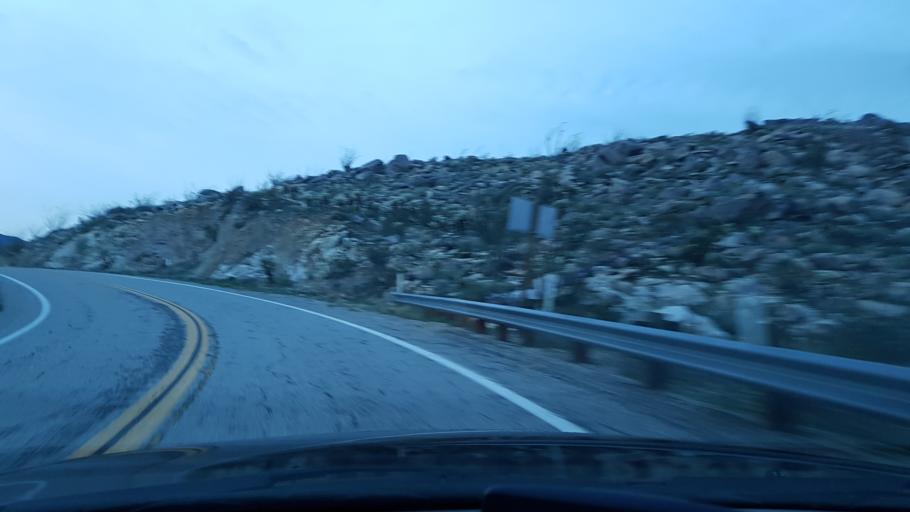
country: US
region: California
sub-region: San Diego County
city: Pine Valley
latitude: 32.9815
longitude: -116.4191
